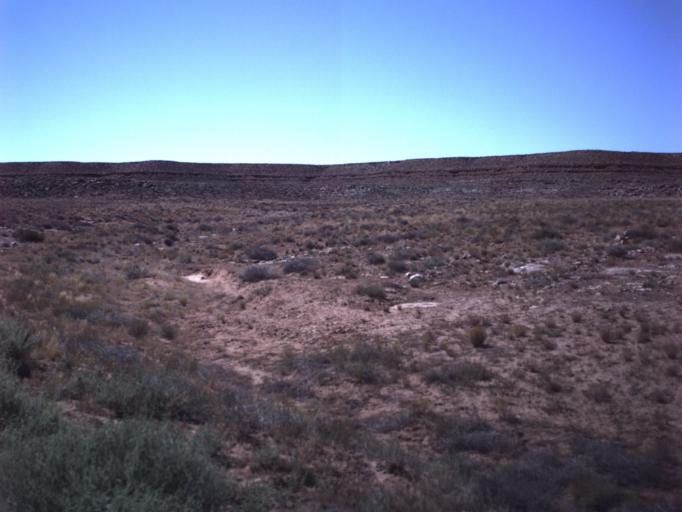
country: US
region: Arizona
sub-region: Navajo County
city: Kayenta
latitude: 37.1873
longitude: -109.9164
